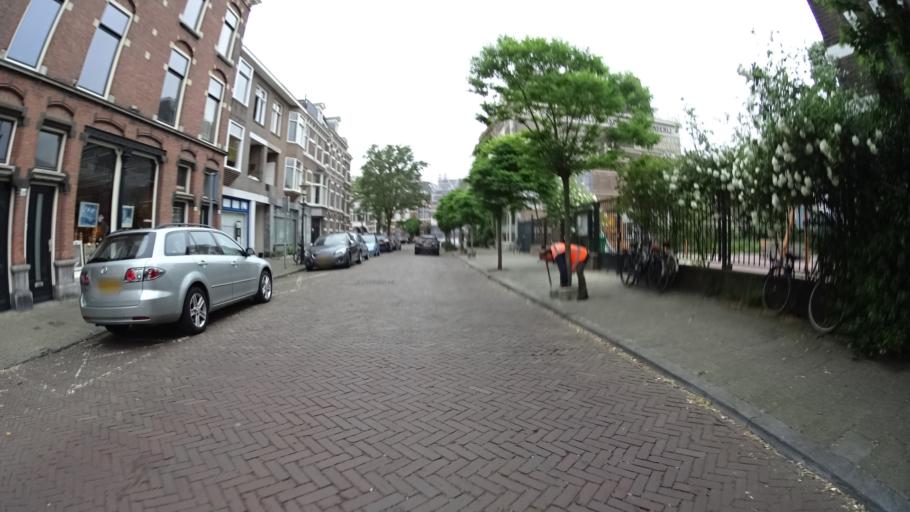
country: NL
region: South Holland
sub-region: Gemeente Den Haag
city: The Hague
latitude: 52.0834
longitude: 4.2899
